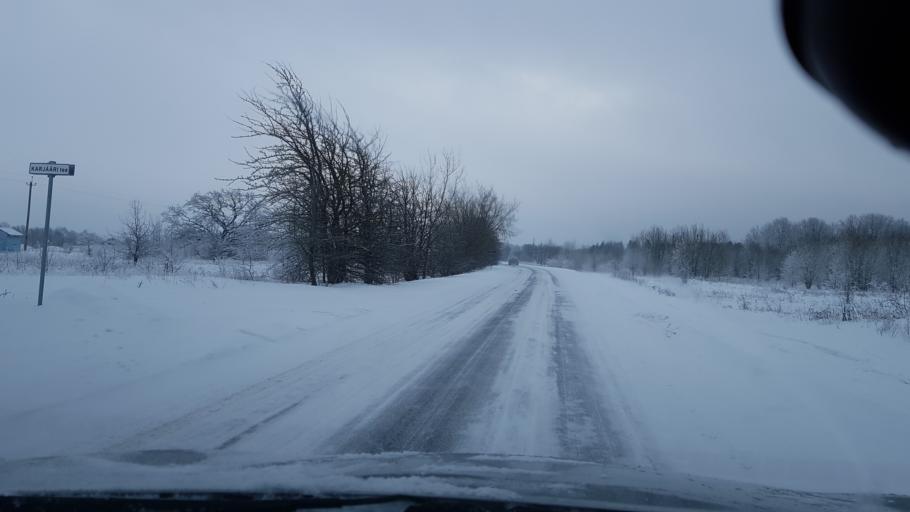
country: EE
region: Harju
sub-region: Keila linn
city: Keila
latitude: 59.3376
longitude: 24.3933
